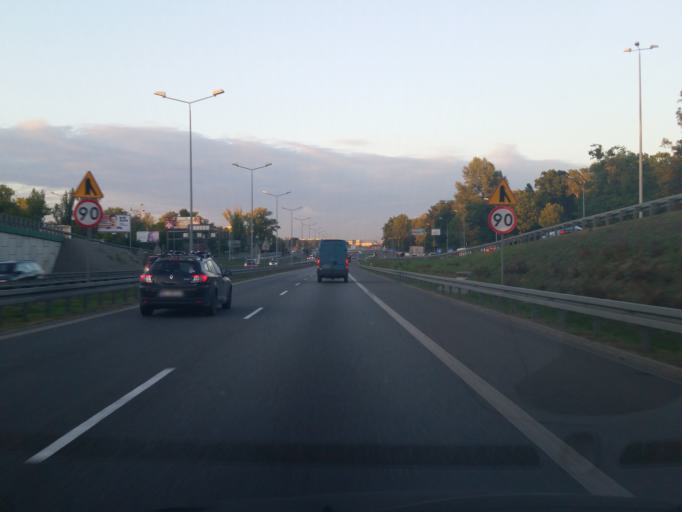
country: PL
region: Masovian Voivodeship
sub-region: Warszawa
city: Bielany
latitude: 52.2573
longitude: 20.9486
